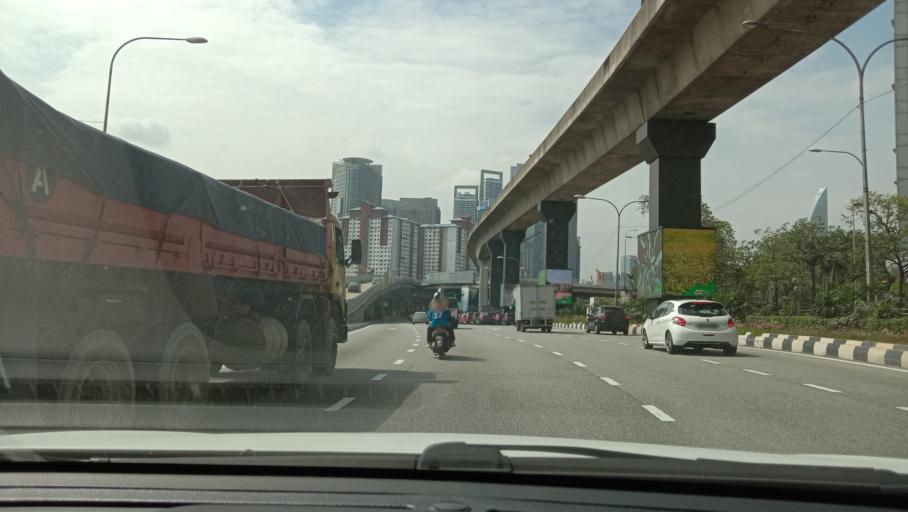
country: MY
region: Kuala Lumpur
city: Kuala Lumpur
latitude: 3.1268
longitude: 101.6786
